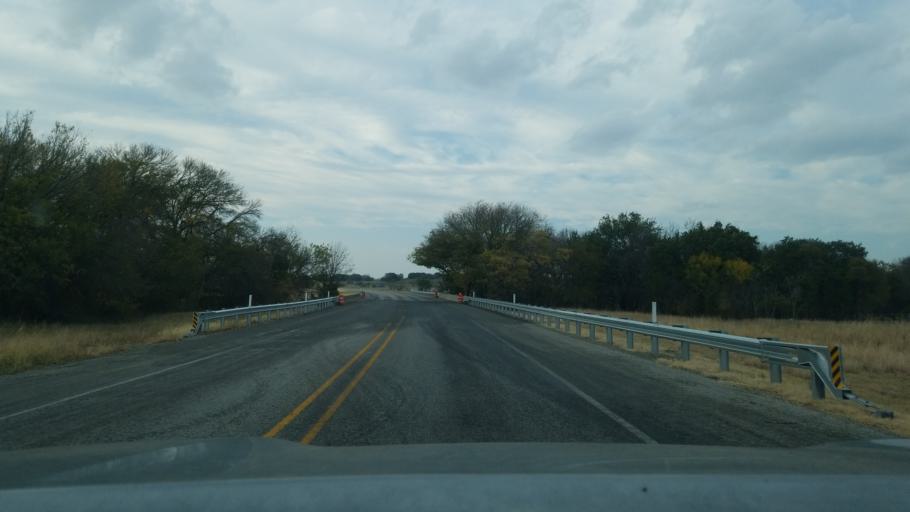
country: US
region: Texas
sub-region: Mills County
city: Goldthwaite
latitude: 31.5129
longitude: -98.5853
